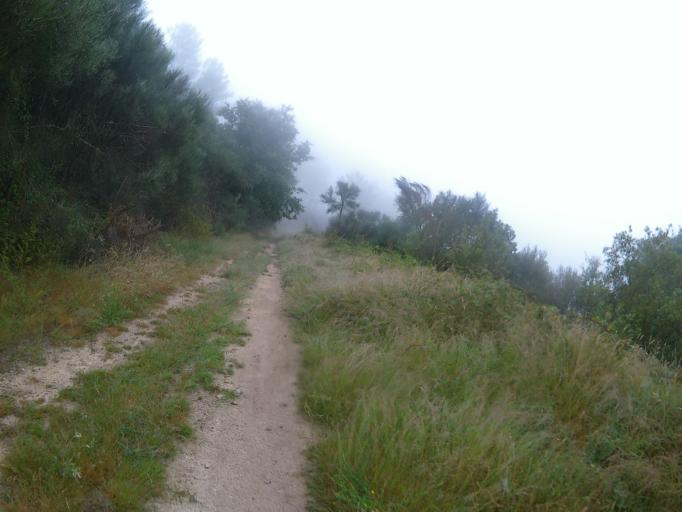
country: PT
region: Viana do Castelo
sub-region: Ponte de Lima
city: Ponte de Lima
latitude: 41.7061
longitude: -8.6034
